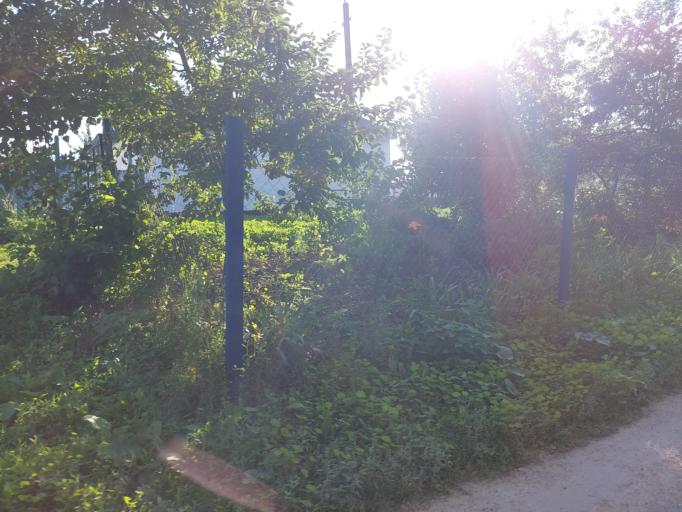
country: RU
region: Lipetsk
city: Terbuny
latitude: 52.2766
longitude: 38.1922
